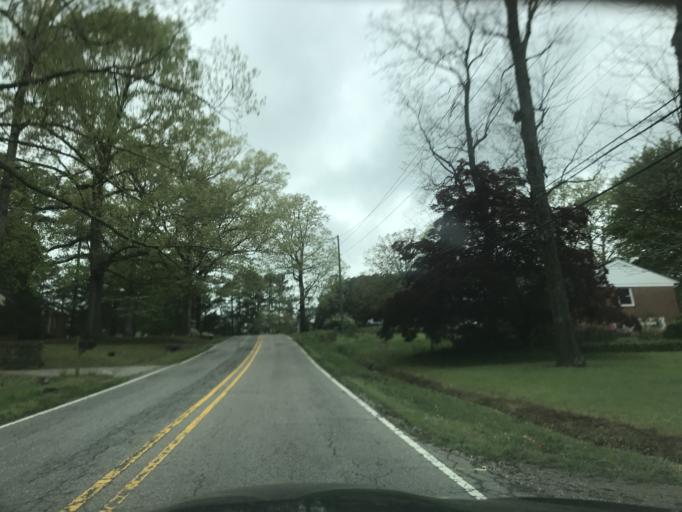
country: US
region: North Carolina
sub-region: Wake County
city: Raleigh
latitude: 35.7518
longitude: -78.6619
